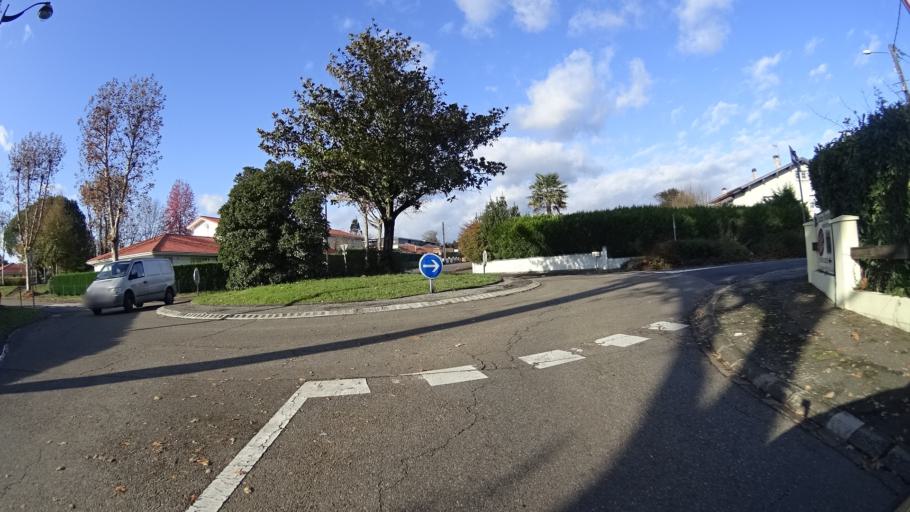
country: FR
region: Aquitaine
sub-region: Departement des Landes
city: Saint-Paul-les-Dax
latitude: 43.7246
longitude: -1.0835
